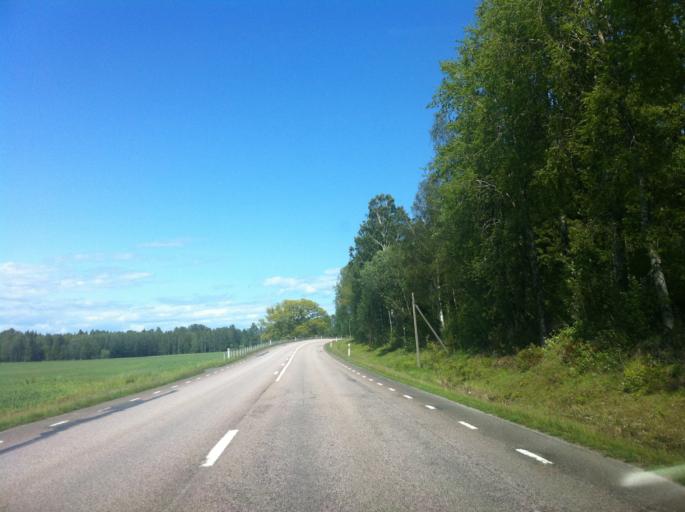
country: SE
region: Vaestra Goetaland
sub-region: Gullspangs Kommun
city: Gullspang
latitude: 59.0070
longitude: 14.1055
